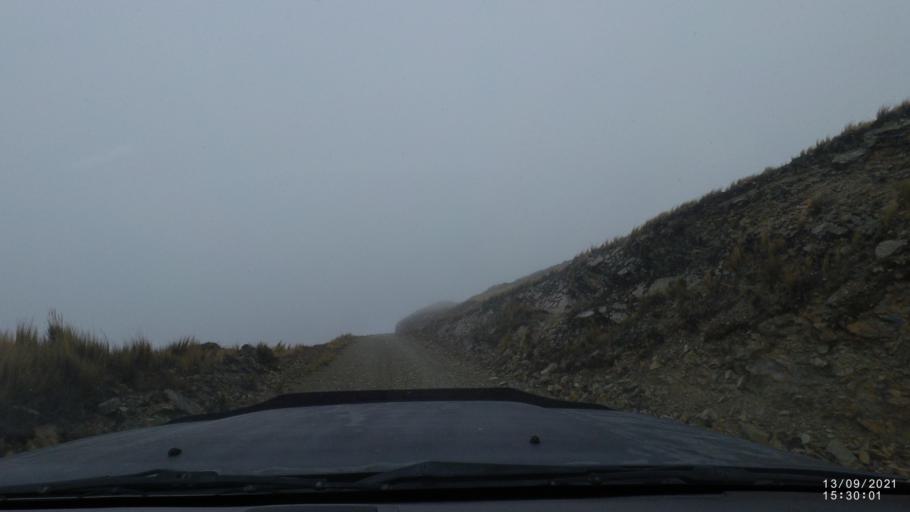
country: BO
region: Cochabamba
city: Colomi
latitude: -17.3445
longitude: -65.7575
